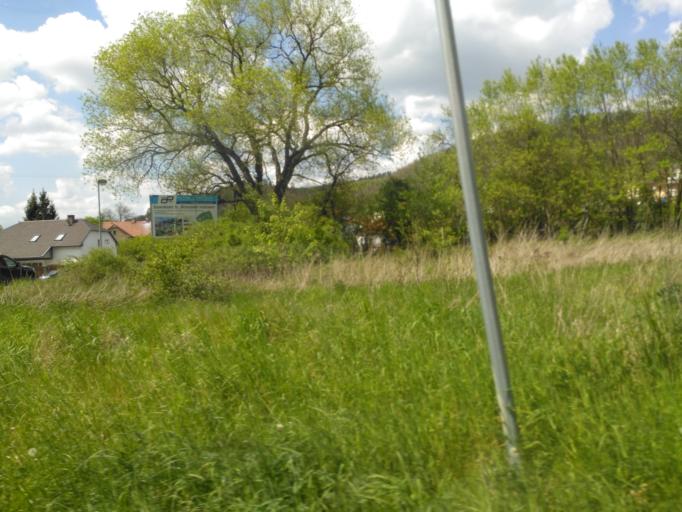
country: CZ
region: Central Bohemia
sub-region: Okres Beroun
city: Kraluv Dvur
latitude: 49.9518
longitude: 14.0294
